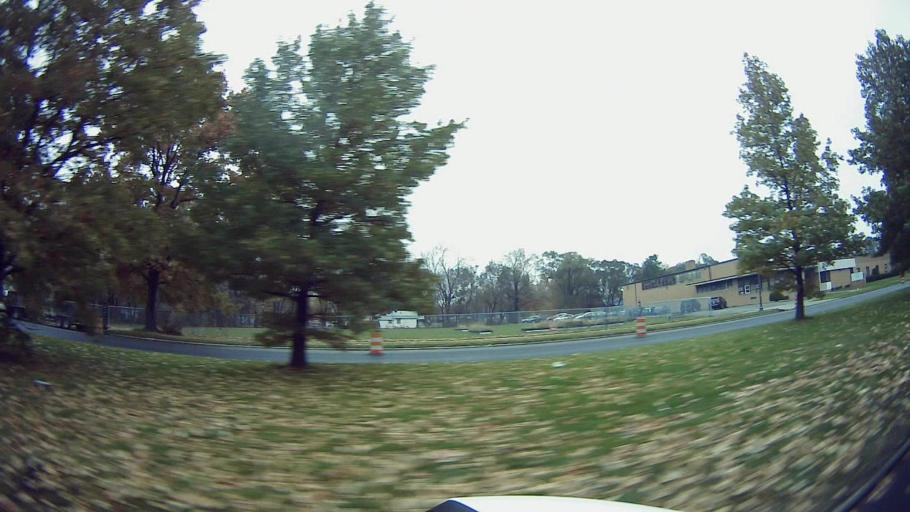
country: US
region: Michigan
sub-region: Oakland County
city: Oak Park
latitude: 42.4194
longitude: -83.2014
